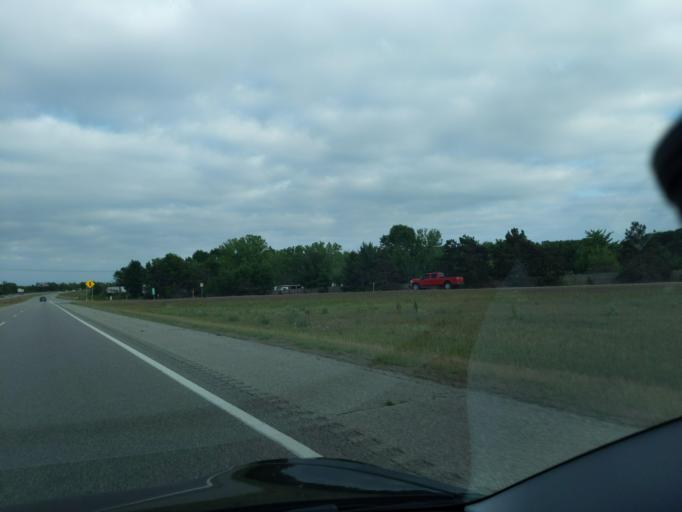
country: US
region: Michigan
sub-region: Muskegon County
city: Lakewood Club
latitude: 43.3208
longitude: -86.2337
